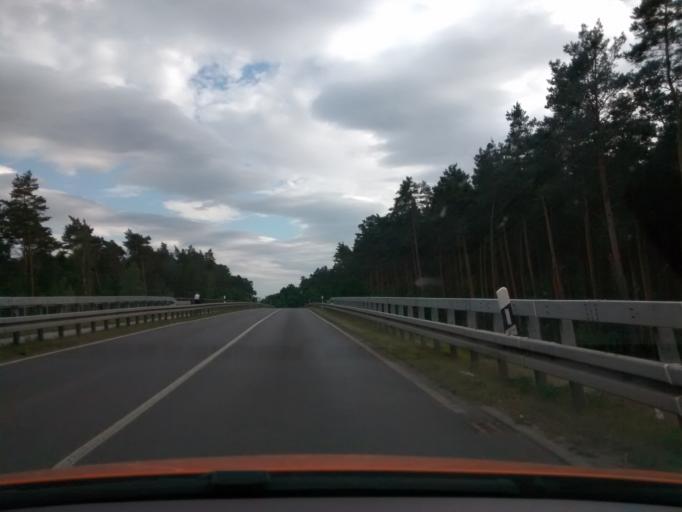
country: DE
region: Berlin
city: Bohnsdorf
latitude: 52.3858
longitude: 13.5689
